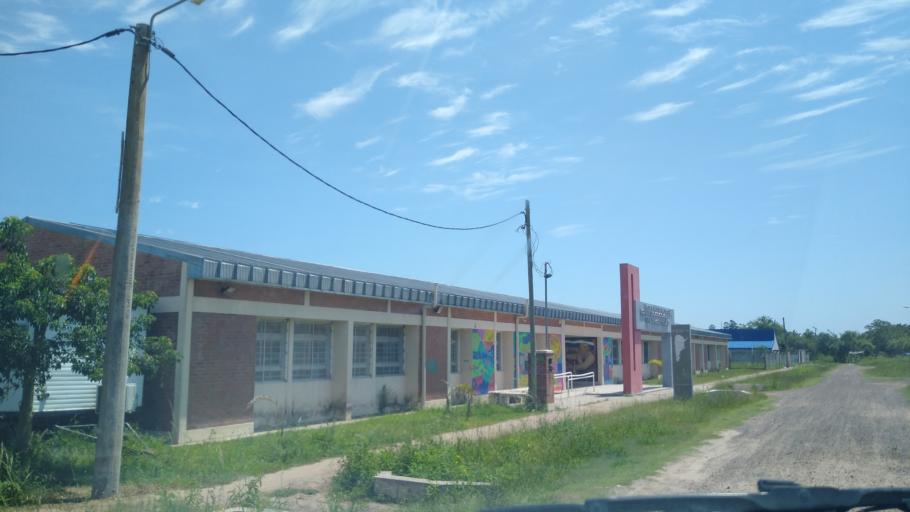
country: AR
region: Chaco
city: Fontana
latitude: -27.4030
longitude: -59.0455
